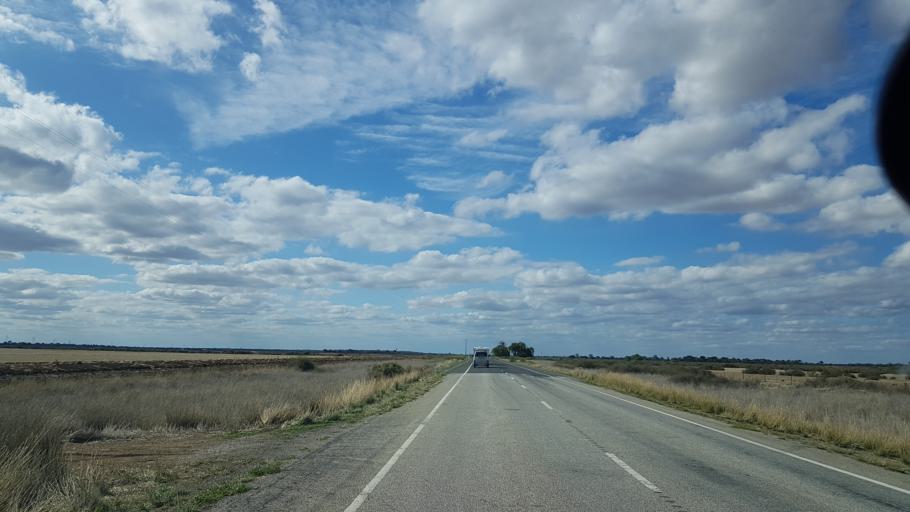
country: AU
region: Victoria
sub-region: Swan Hill
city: Swan Hill
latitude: -35.8521
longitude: 143.9369
